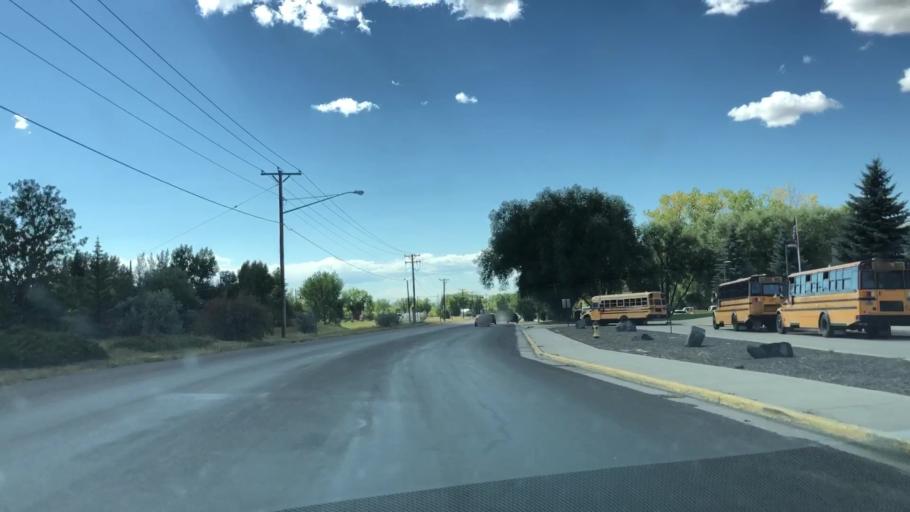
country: US
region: Wyoming
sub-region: Albany County
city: Laramie
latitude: 41.3028
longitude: -105.5823
